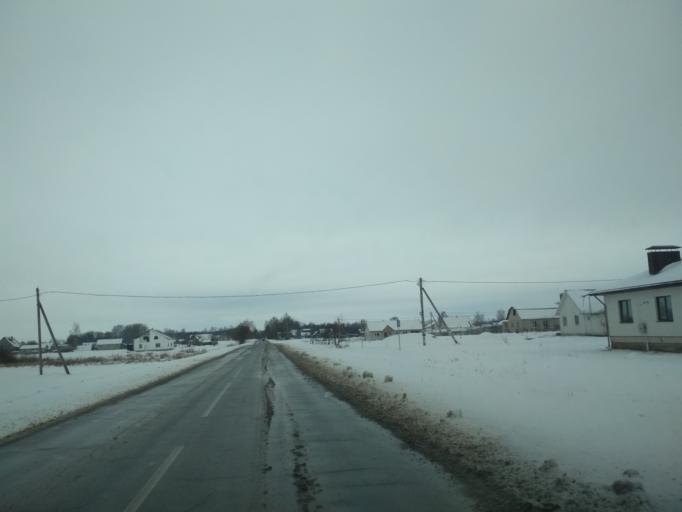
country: BY
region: Minsk
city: Mar''ina Horka
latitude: 53.5106
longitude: 28.1037
